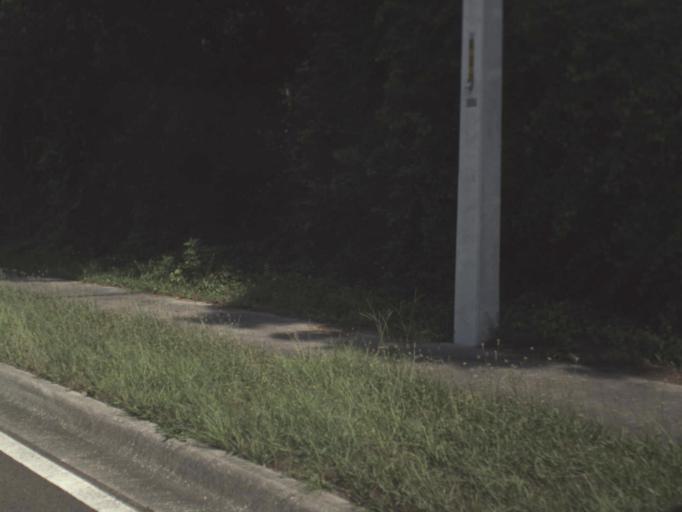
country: US
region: Florida
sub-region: Clay County
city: Bellair-Meadowbrook Terrace
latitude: 30.2473
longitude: -81.8346
